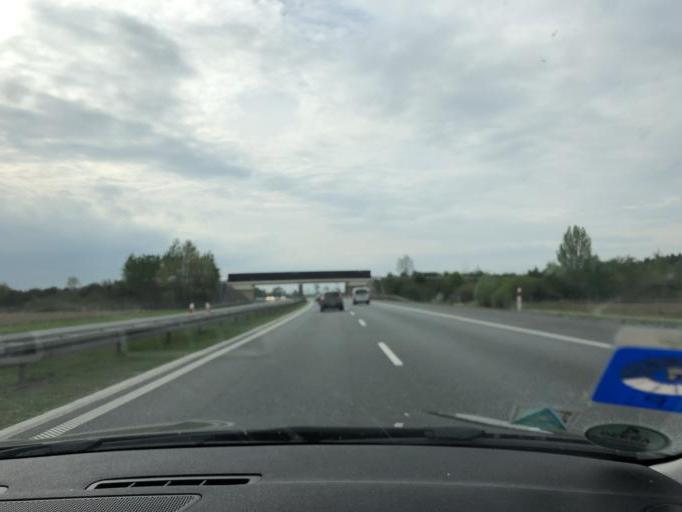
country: PL
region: Opole Voivodeship
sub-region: Powiat brzeski
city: Lewin Brzeski
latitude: 50.7057
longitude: 17.6124
